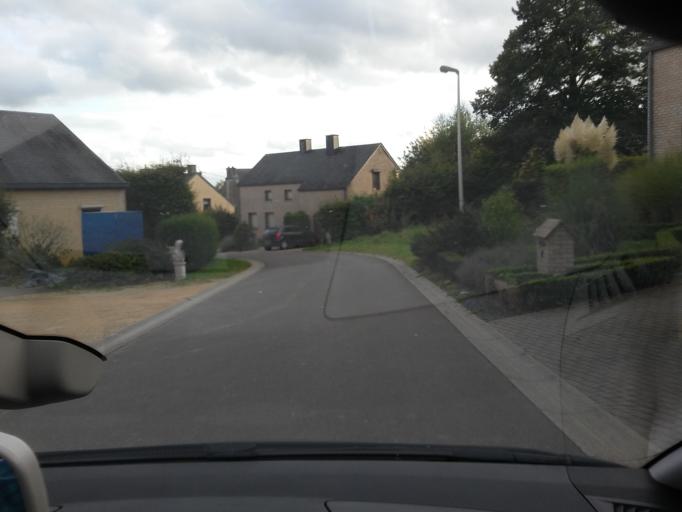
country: BE
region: Wallonia
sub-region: Province du Luxembourg
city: Arlon
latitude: 49.6991
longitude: 5.7691
